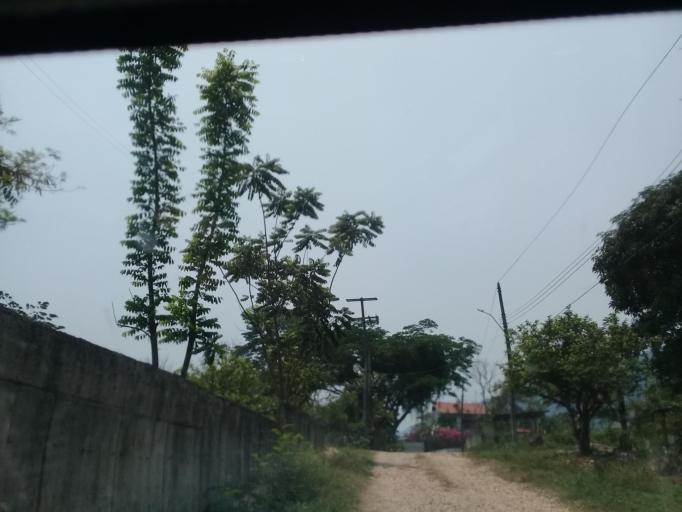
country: MX
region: Veracruz
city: Tezonapa
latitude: 18.6084
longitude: -96.6882
